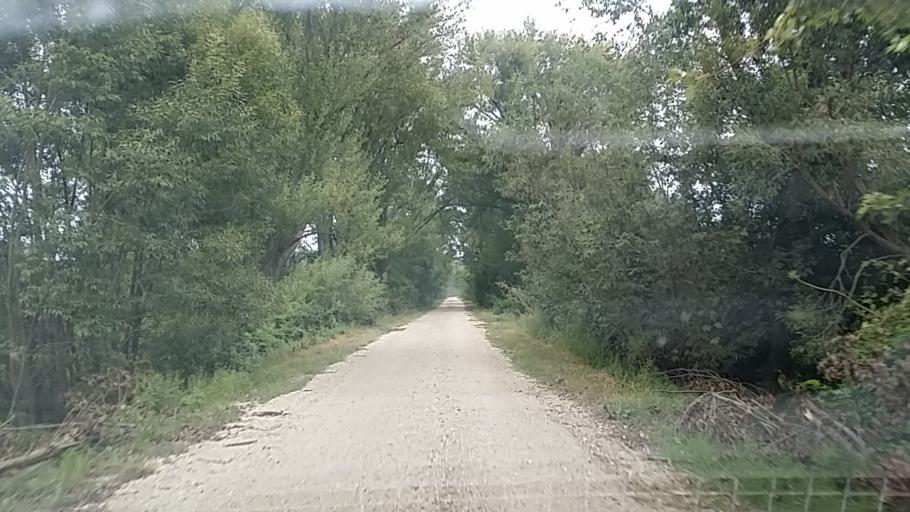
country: HU
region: Gyor-Moson-Sopron
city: Farad
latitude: 47.6638
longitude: 17.1380
